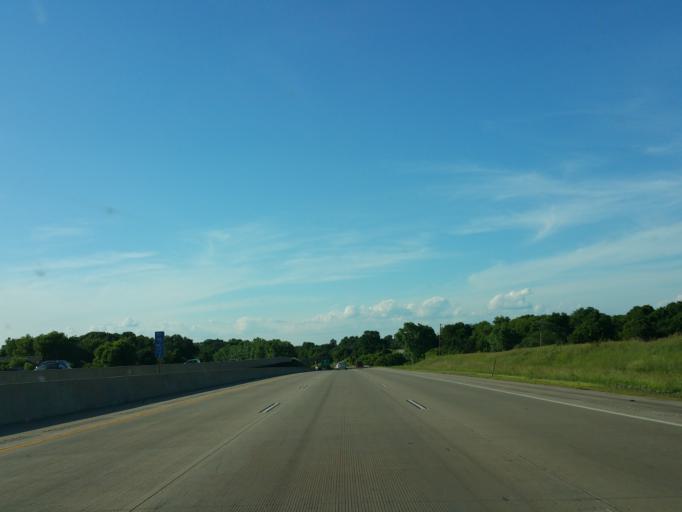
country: US
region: Wisconsin
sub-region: Columbia County
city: Poynette
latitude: 43.3721
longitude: -89.4601
